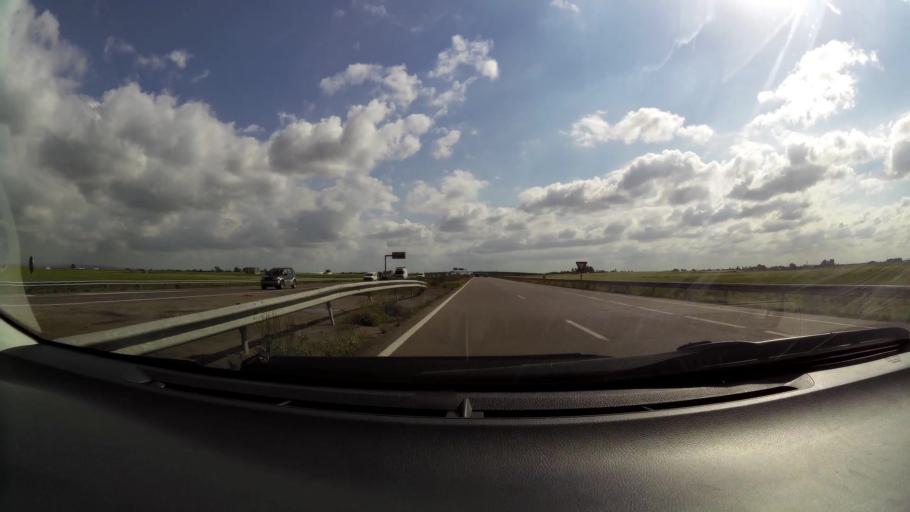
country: MA
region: Chaouia-Ouardigha
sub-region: Settat Province
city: Berrechid
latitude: 33.2439
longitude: -7.5664
